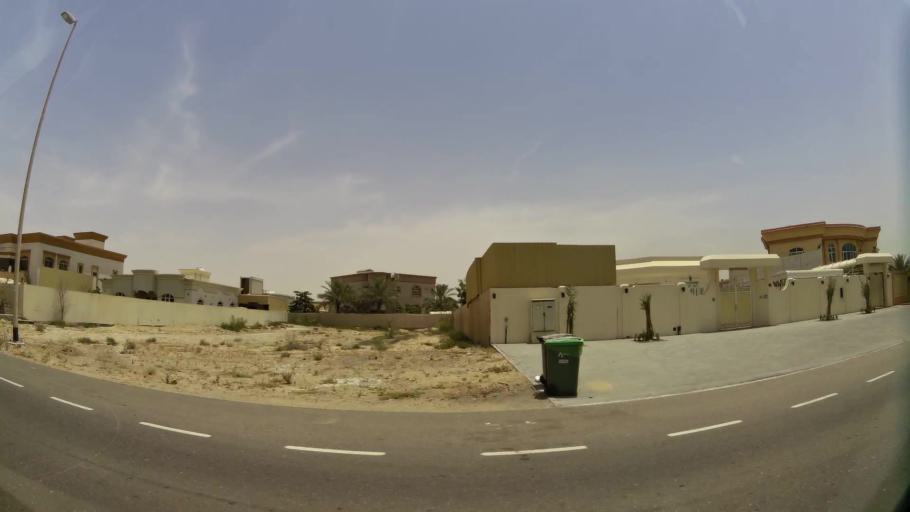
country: AE
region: Ash Shariqah
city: Sharjah
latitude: 25.2520
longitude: 55.4590
